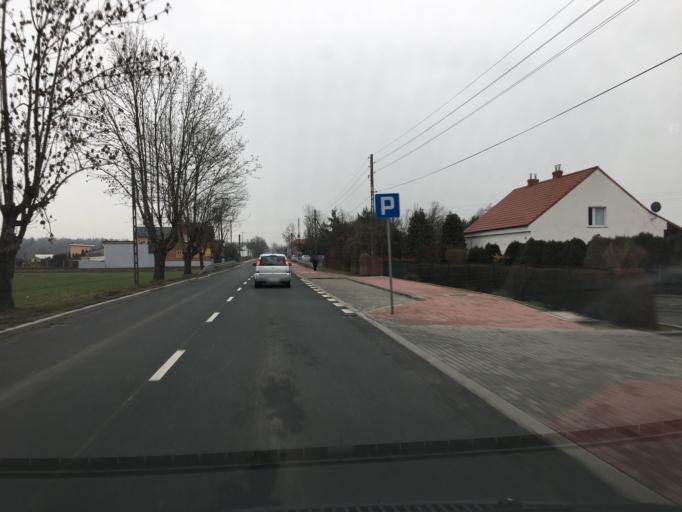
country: PL
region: Opole Voivodeship
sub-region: Powiat kedzierzynsko-kozielski
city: Bierawa
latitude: 50.3121
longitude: 18.2263
